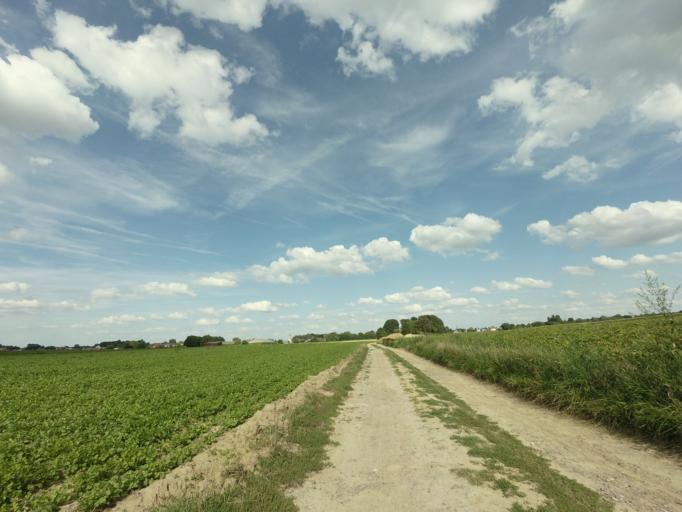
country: BE
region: Flanders
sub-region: Provincie Vlaams-Brabant
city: Grimbergen
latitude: 50.9480
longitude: 4.3549
